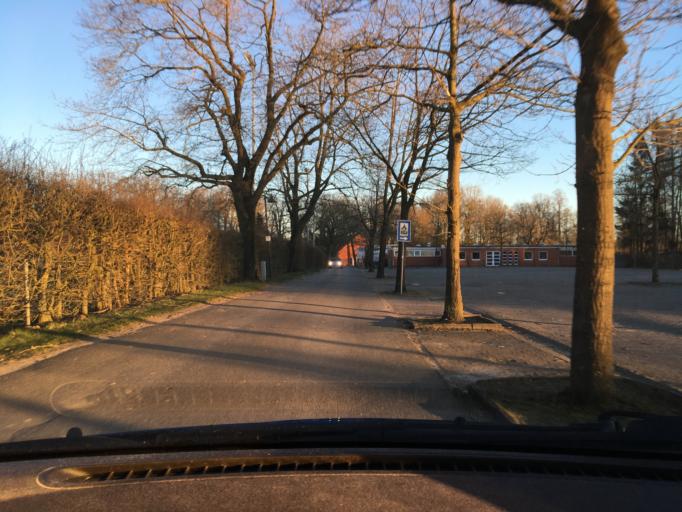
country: DE
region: Lower Saxony
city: Dahlenburg
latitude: 53.1833
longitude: 10.7482
